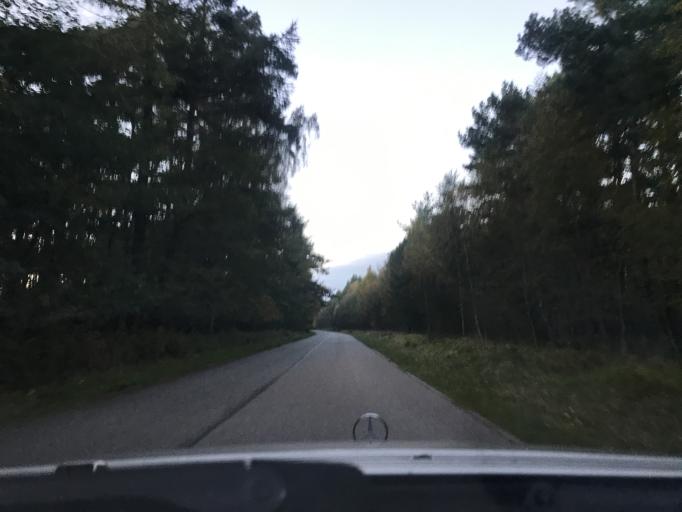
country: DE
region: Mecklenburg-Vorpommern
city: Karlshagen
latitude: 54.1454
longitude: 13.8093
